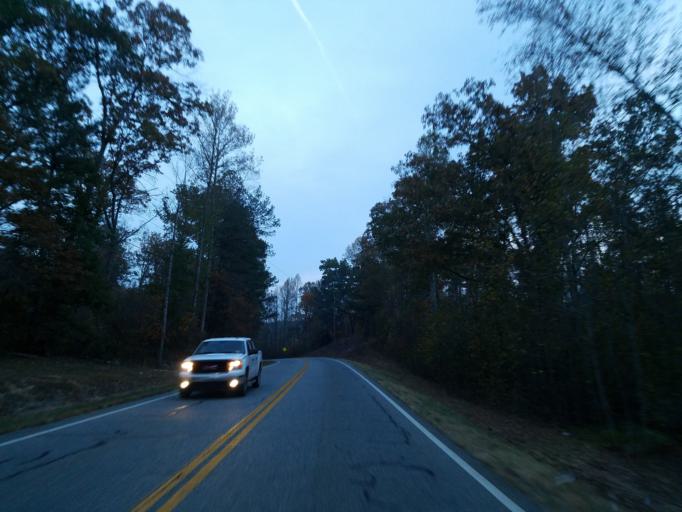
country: US
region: Georgia
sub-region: Gilmer County
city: Ellijay
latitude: 34.5520
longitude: -84.5999
